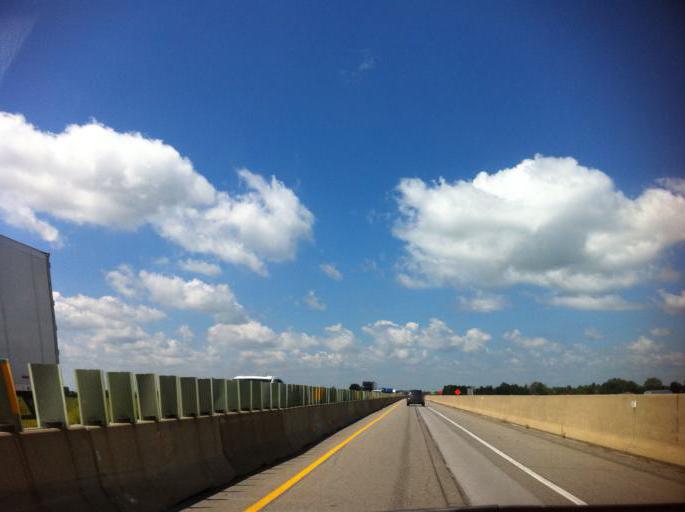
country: US
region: Ohio
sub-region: Sandusky County
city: Clyde
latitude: 41.3610
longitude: -82.9237
